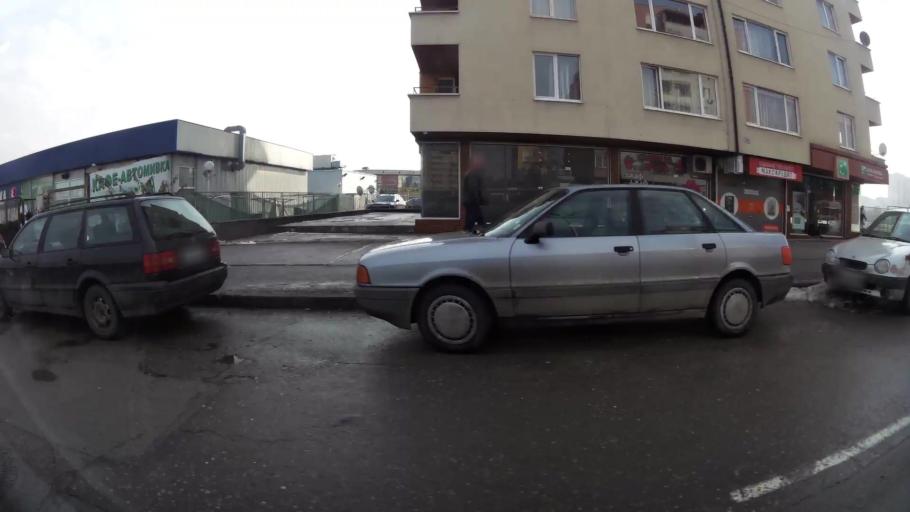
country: BG
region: Sofiya
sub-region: Obshtina Bozhurishte
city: Bozhurishte
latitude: 42.7184
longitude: 23.2537
